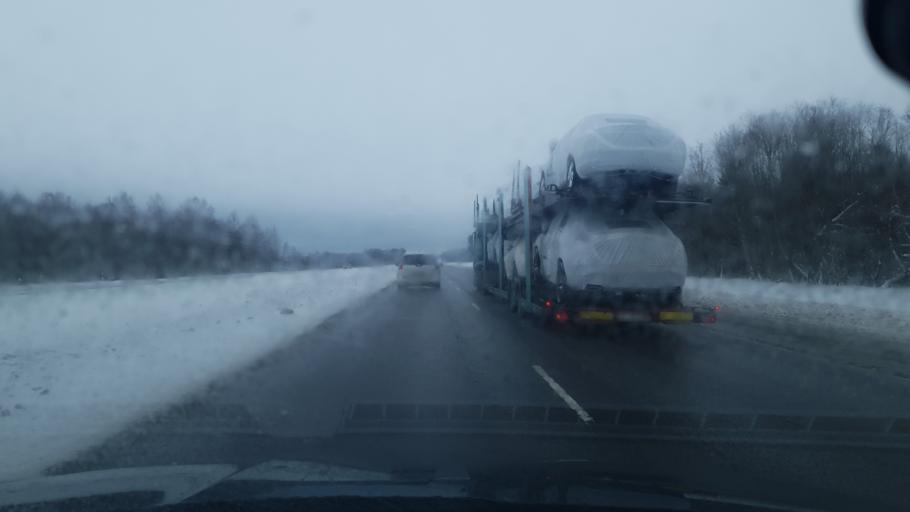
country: EE
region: Harju
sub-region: Rae vald
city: Vaida
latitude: 59.2686
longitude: 24.9933
